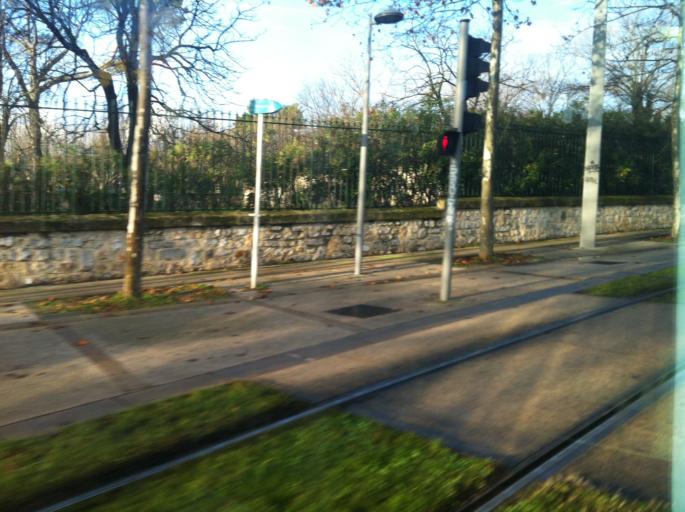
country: FR
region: Languedoc-Roussillon
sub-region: Departement de l'Herault
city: Montpellier
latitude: 43.6281
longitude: 3.8577
